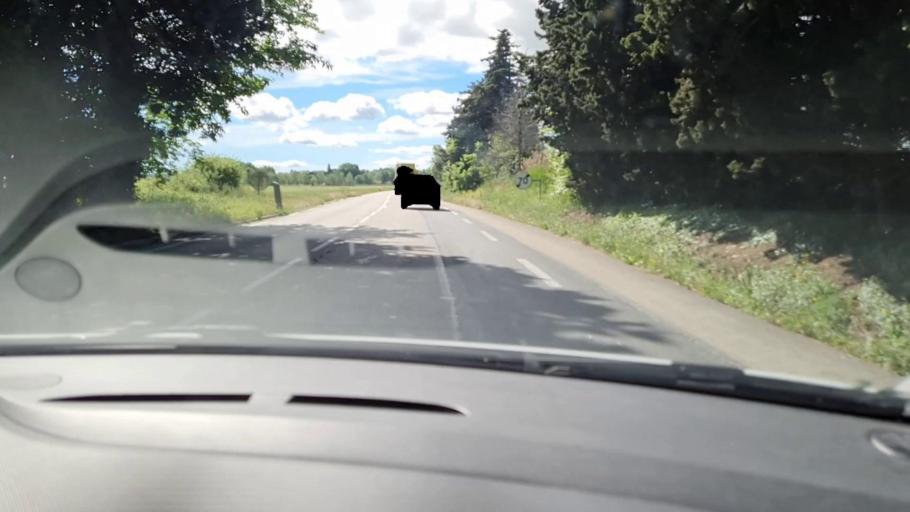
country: FR
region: Languedoc-Roussillon
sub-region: Departement du Gard
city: Milhaud
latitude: 43.7968
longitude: 4.3439
